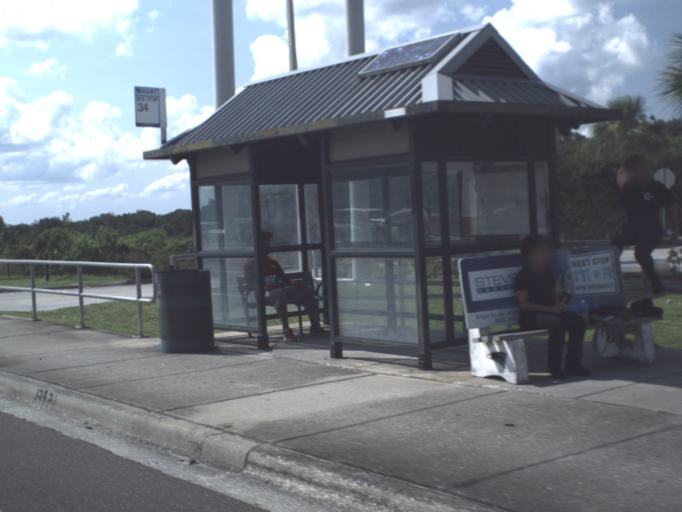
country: US
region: Florida
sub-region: Hillsborough County
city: Egypt Lake-Leto
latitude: 27.9963
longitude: -82.4641
